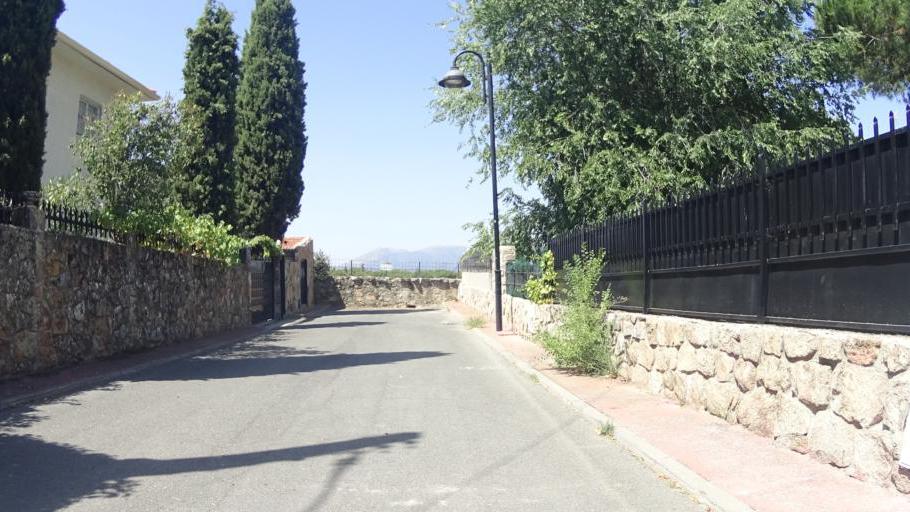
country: ES
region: Madrid
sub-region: Provincia de Madrid
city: Galapagar
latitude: 40.5728
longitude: -4.0100
